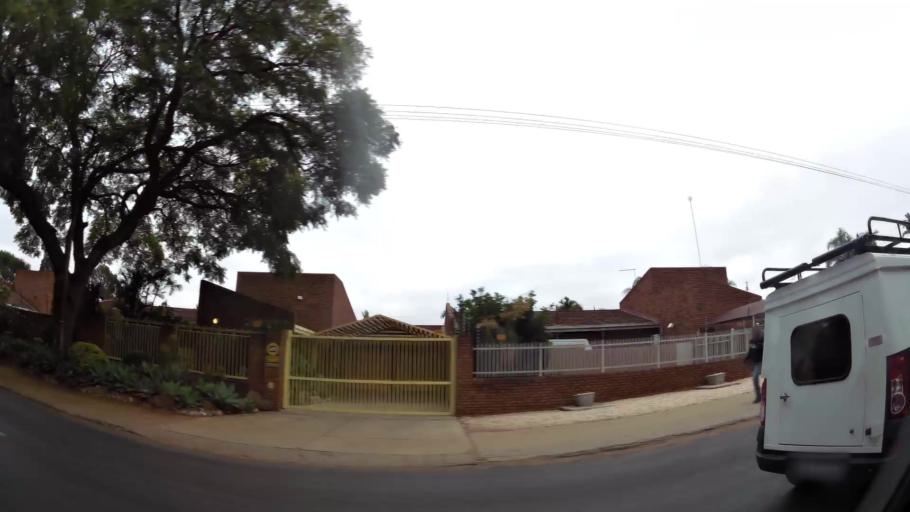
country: ZA
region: Limpopo
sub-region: Capricorn District Municipality
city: Polokwane
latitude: -23.9014
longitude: 29.4570
